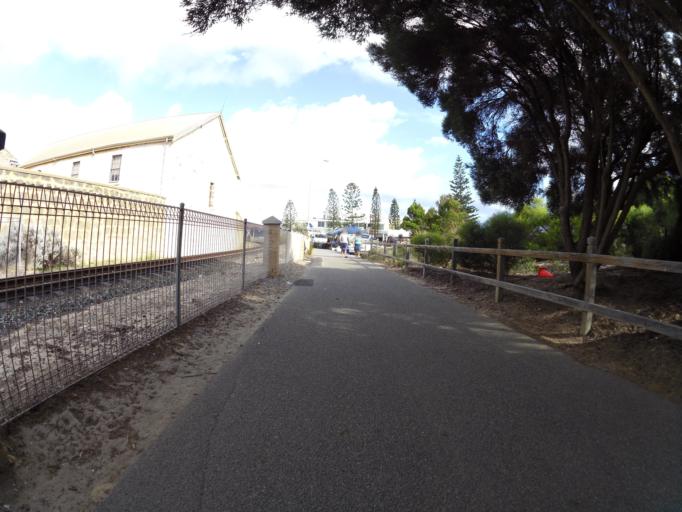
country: AU
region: Western Australia
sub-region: Fremantle
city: South Fremantle
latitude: -32.0570
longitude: 115.7419
